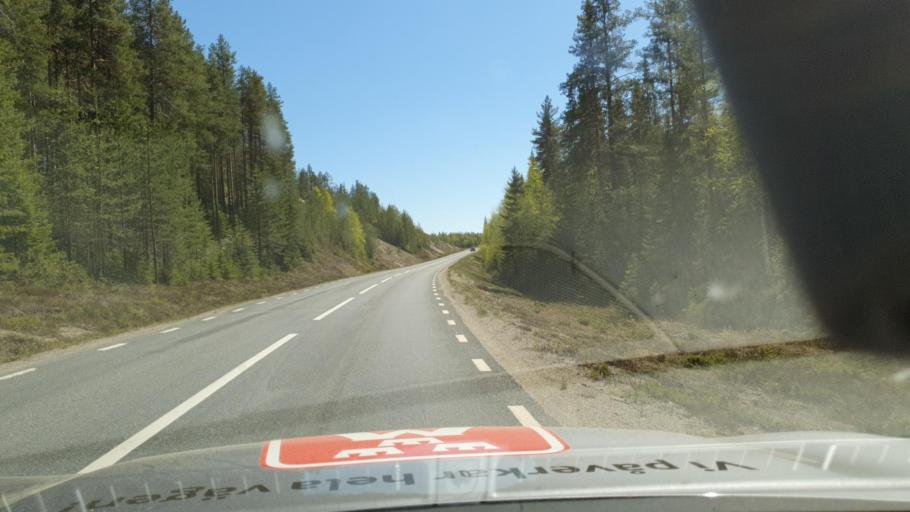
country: SE
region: Vaesternorrland
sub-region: OErnskoeldsviks Kommun
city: Bredbyn
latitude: 63.7998
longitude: 18.4973
